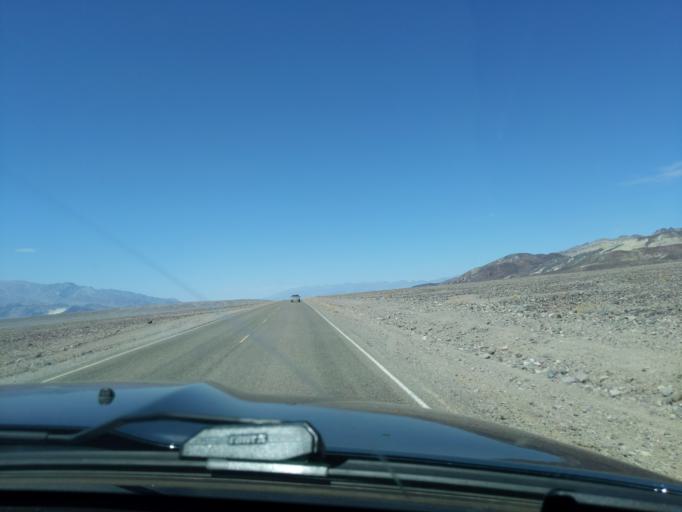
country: US
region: Nevada
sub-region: Nye County
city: Beatty
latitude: 36.3091
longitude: -116.8168
